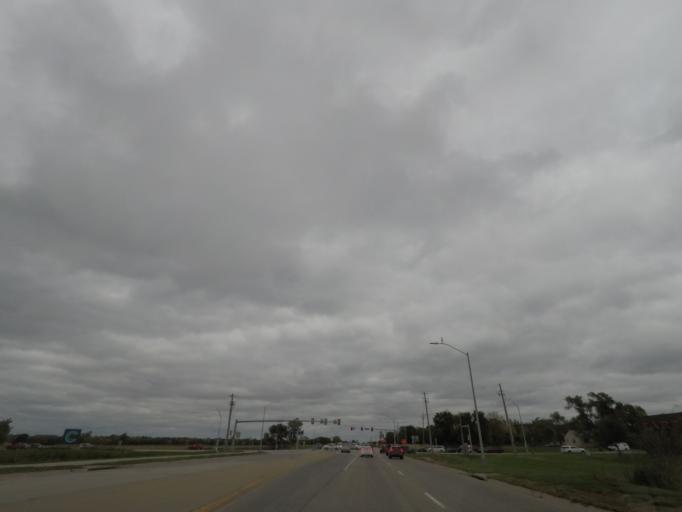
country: US
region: Iowa
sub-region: Polk County
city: Ankeny
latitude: 41.7019
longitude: -93.6005
